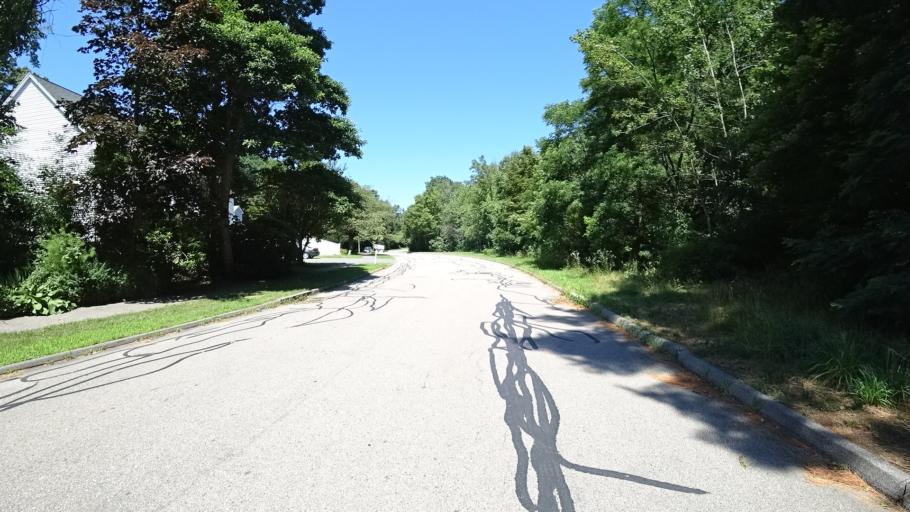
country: US
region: Massachusetts
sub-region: Norfolk County
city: Dedham
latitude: 42.2281
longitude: -71.1893
